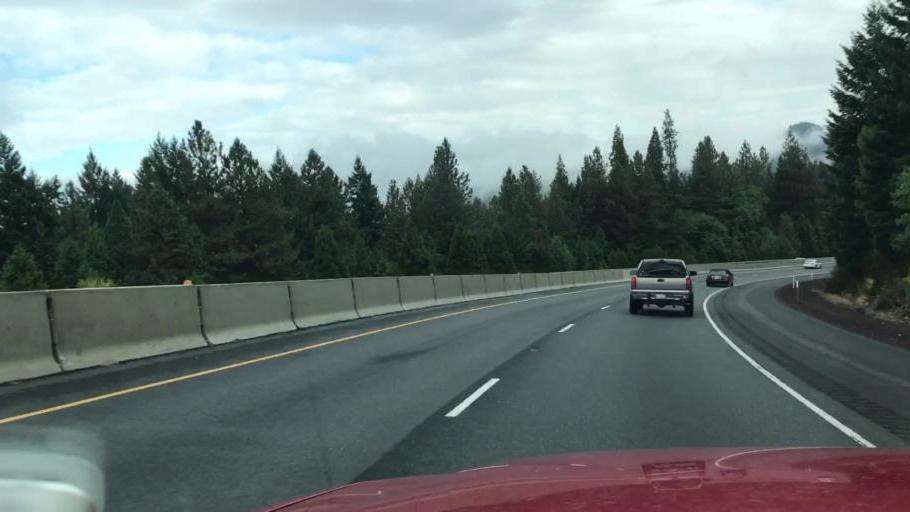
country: US
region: Oregon
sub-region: Josephine County
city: Merlin
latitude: 42.6245
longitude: -123.3839
